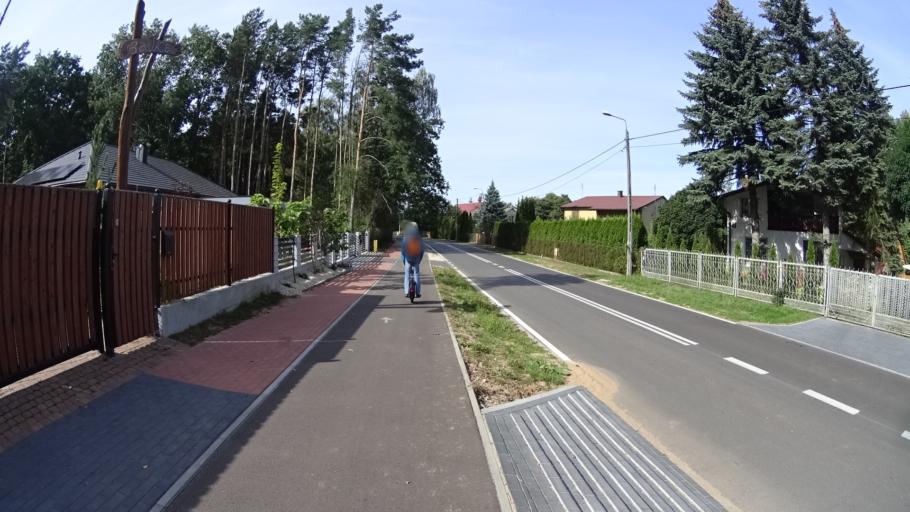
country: PL
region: Masovian Voivodeship
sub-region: Powiat legionowski
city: Bialobrzegi
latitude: 52.4708
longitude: 21.0722
